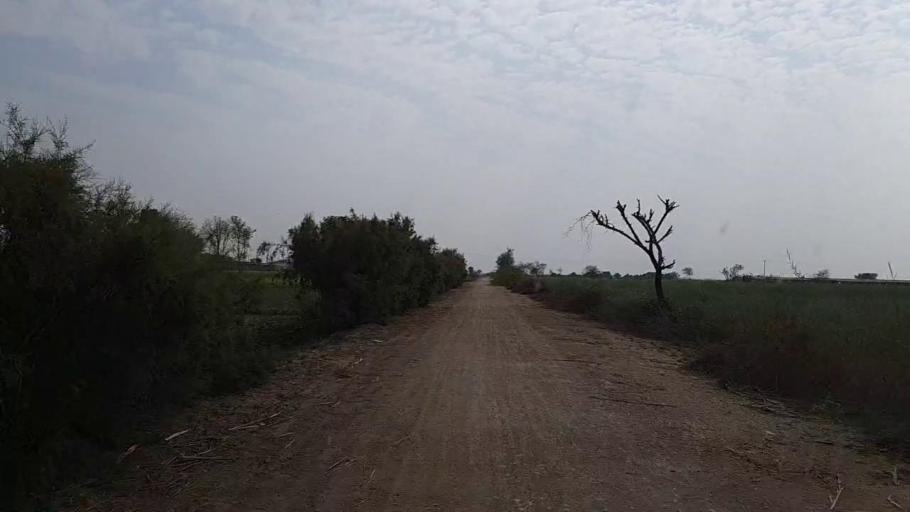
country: PK
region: Sindh
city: Mirwah Gorchani
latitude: 25.3945
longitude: 69.1018
